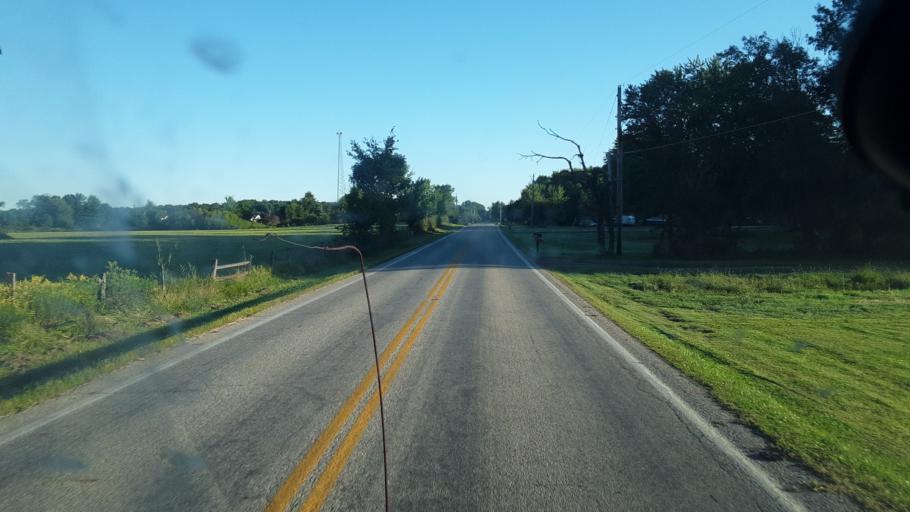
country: US
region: Ohio
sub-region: Trumbull County
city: South Canal
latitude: 41.1618
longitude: -81.0512
